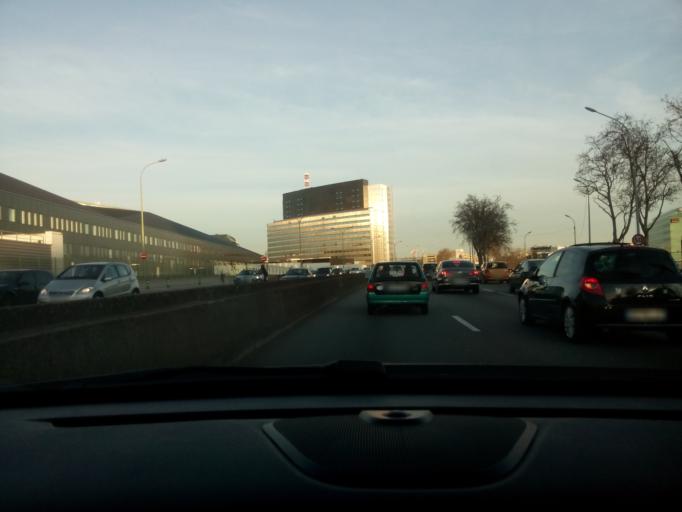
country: FR
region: Ile-de-France
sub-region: Departement des Hauts-de-Seine
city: Issy-les-Moulineaux
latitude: 48.8349
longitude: 2.2739
